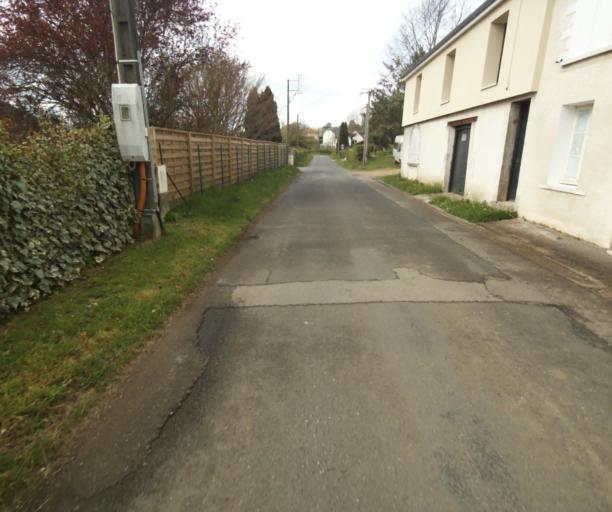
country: FR
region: Limousin
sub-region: Departement de la Correze
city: Tulle
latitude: 45.2768
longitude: 1.7475
